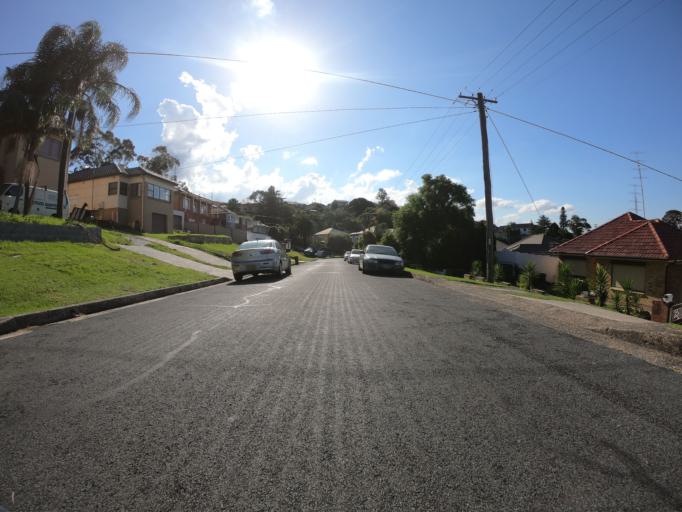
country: AU
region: New South Wales
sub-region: Wollongong
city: West Wollongong
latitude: -34.4345
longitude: 150.8585
